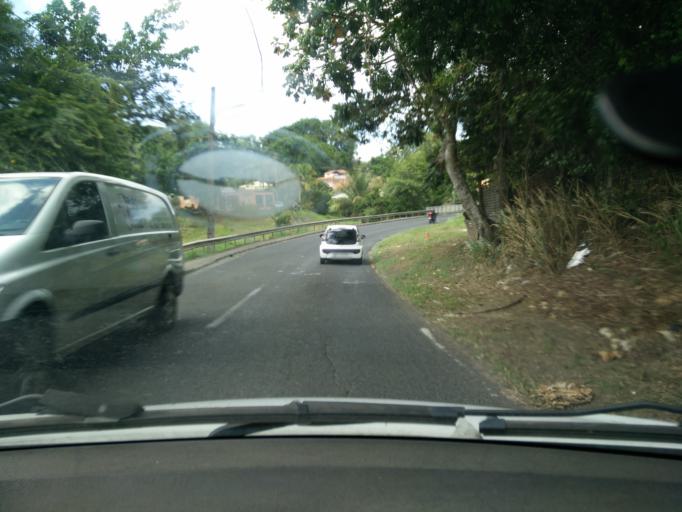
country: GP
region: Guadeloupe
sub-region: Guadeloupe
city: Les Abymes
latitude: 16.2618
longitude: -61.4970
